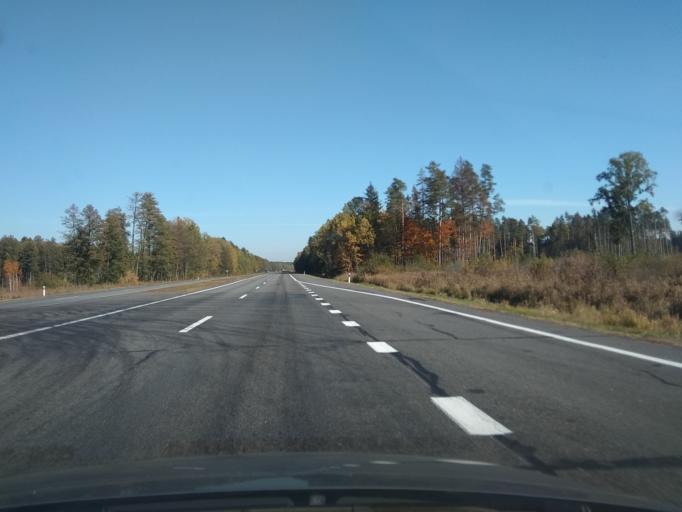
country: BY
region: Brest
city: Nyakhachava
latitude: 52.6399
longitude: 25.2300
